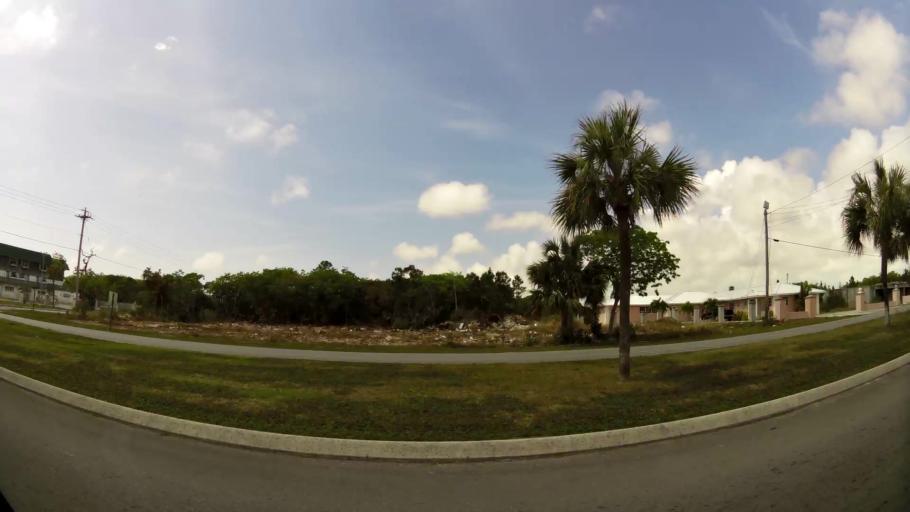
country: BS
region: Freeport
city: Freeport
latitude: 26.5019
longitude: -78.7002
